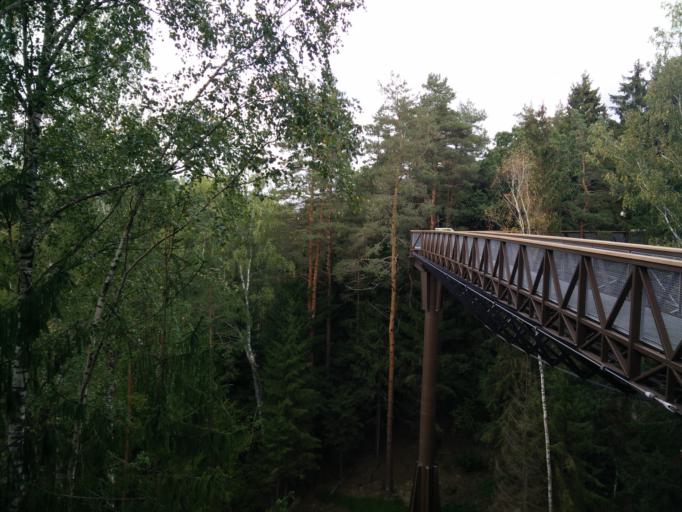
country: LT
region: Utenos apskritis
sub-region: Anyksciai
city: Anyksciai
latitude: 55.4854
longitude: 25.0612
